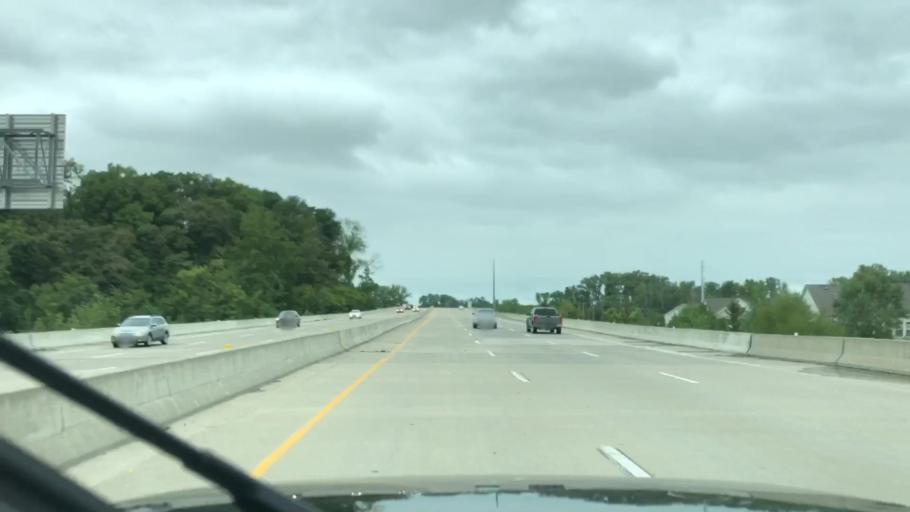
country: US
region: Missouri
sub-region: Saint Louis County
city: Maryland Heights
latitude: 38.6900
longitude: -90.4968
